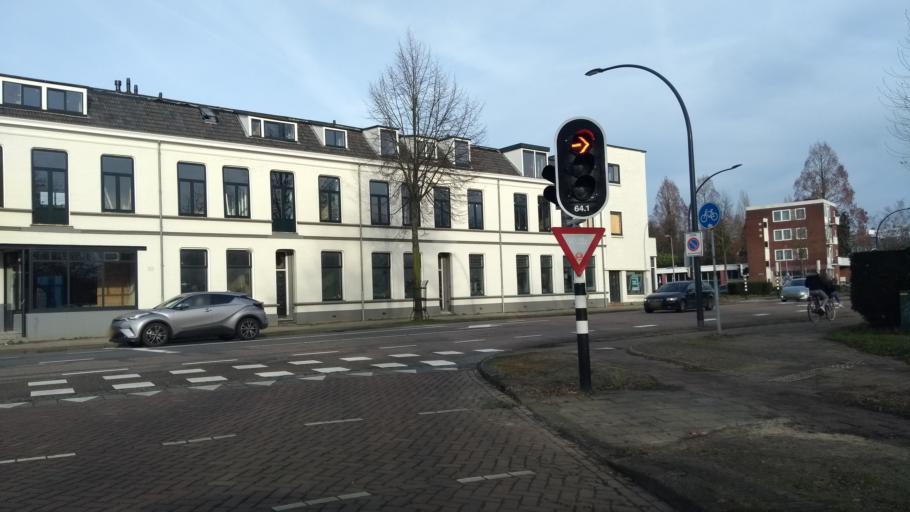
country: NL
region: Overijssel
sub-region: Gemeente Hengelo
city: Hengelo
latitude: 52.2661
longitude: 6.7859
